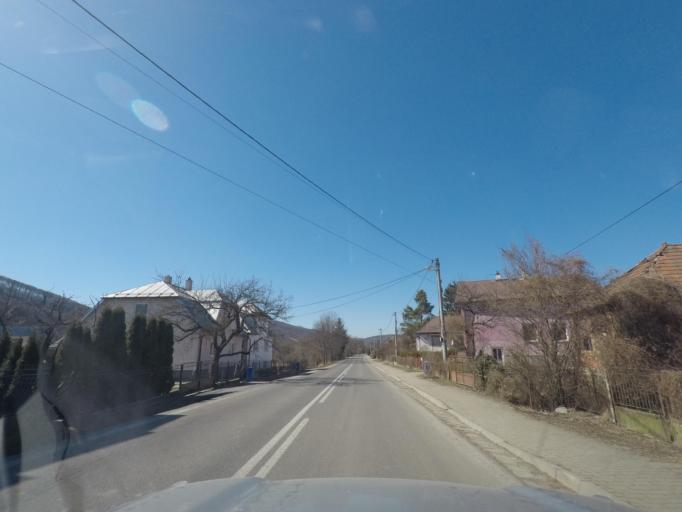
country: UA
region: Zakarpattia
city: Velykyi Bereznyi
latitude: 48.8939
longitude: 22.4068
